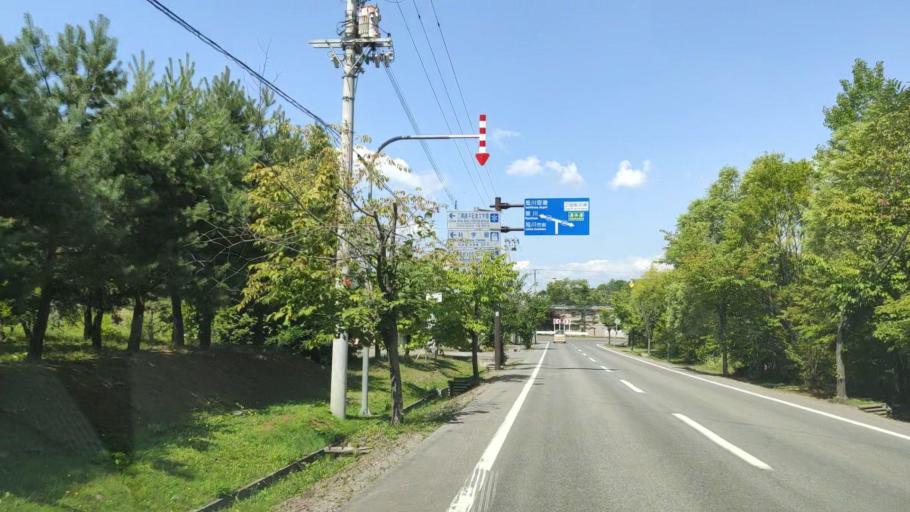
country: JP
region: Hokkaido
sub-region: Asahikawa-shi
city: Asahikawa
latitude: 43.7719
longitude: 142.4779
